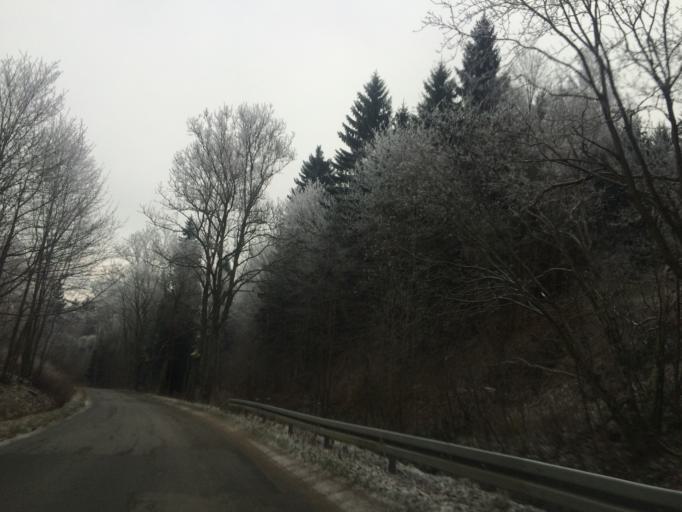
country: PL
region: Lower Silesian Voivodeship
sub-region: Powiat klodzki
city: Stronie Slaskie
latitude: 50.2682
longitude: 16.8398
